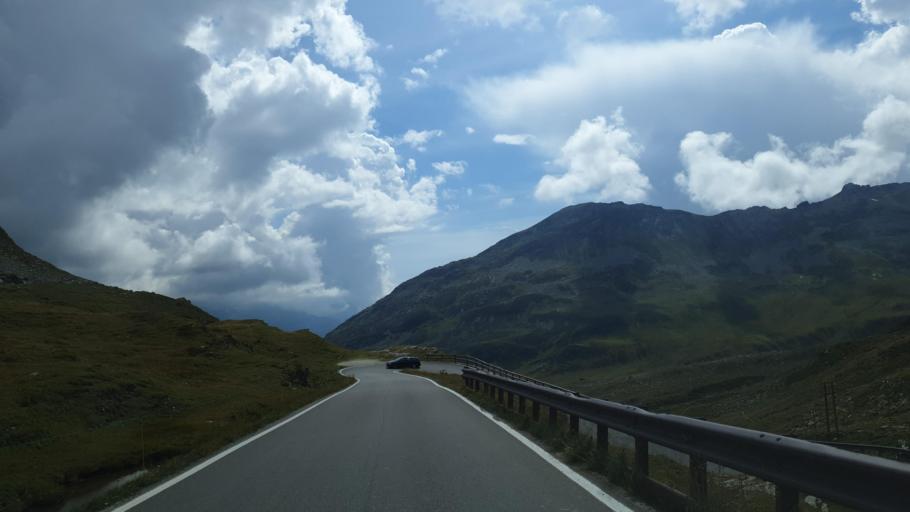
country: IT
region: Lombardy
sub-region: Provincia di Sondrio
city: Campodolcino
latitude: 46.4986
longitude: 9.3302
